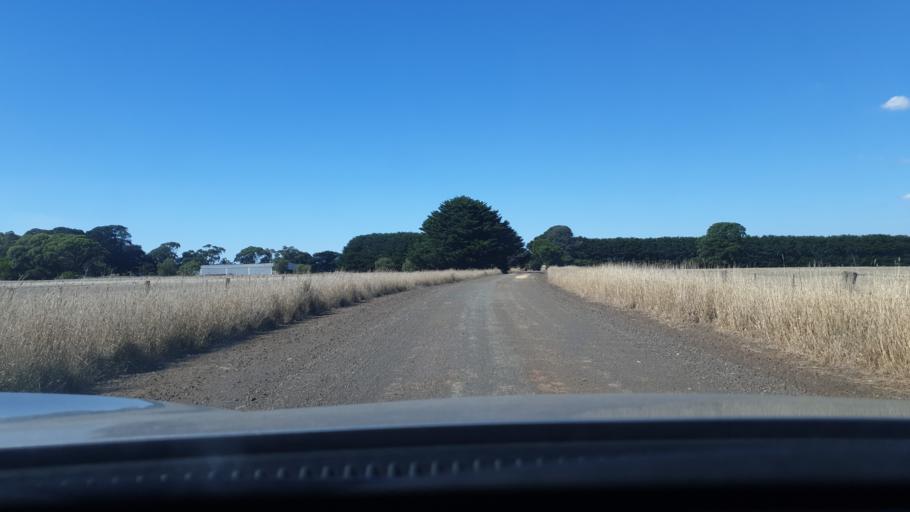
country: AU
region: Victoria
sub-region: Warrnambool
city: Warrnambool
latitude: -38.1651
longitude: 142.3726
